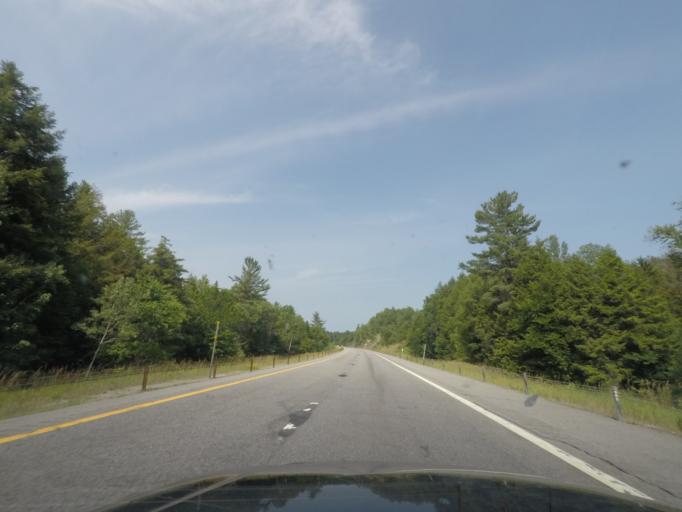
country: US
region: New York
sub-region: Essex County
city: Mineville
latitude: 44.1200
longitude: -73.5979
